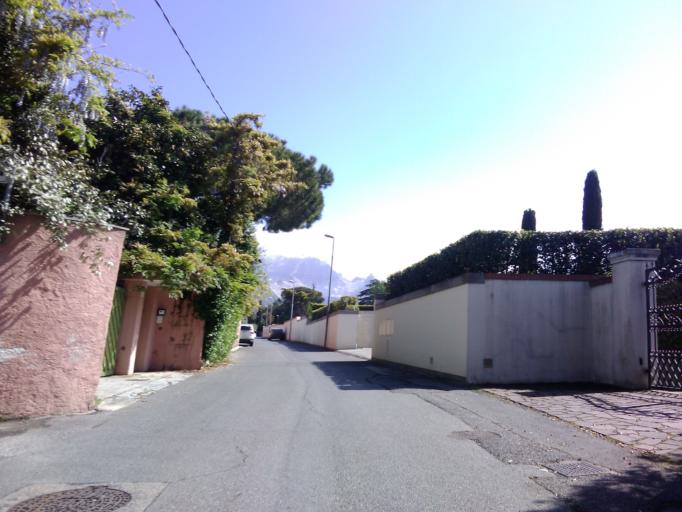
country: IT
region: Tuscany
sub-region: Provincia di Massa-Carrara
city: Carrara
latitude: 44.0606
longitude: 10.0647
